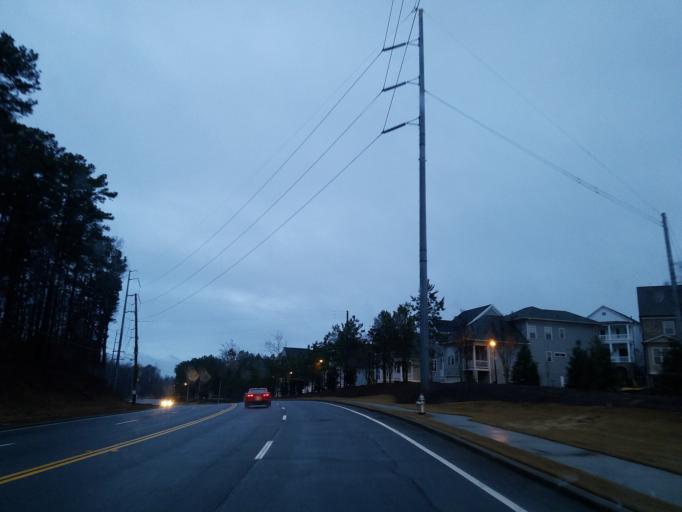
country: US
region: Georgia
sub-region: Fulton County
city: Roswell
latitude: 34.0066
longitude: -84.2981
